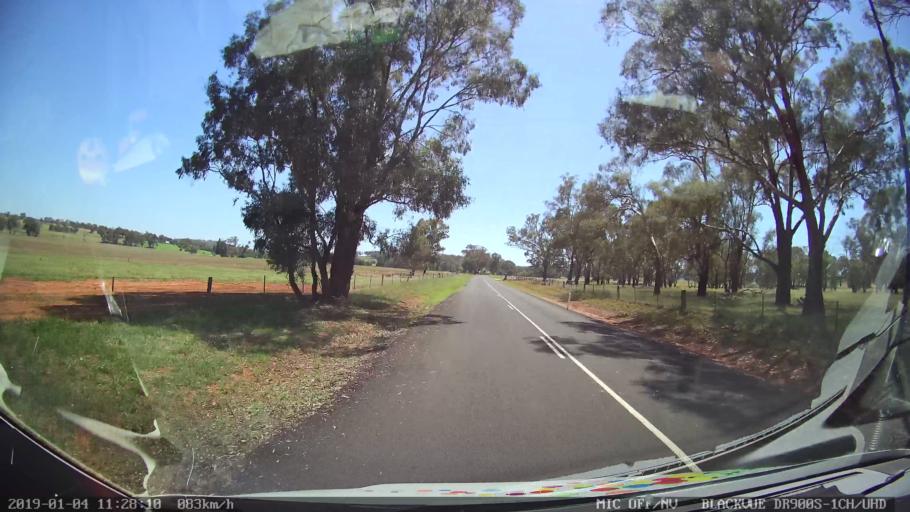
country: AU
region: New South Wales
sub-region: Cabonne
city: Molong
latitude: -33.1023
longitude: 148.7695
